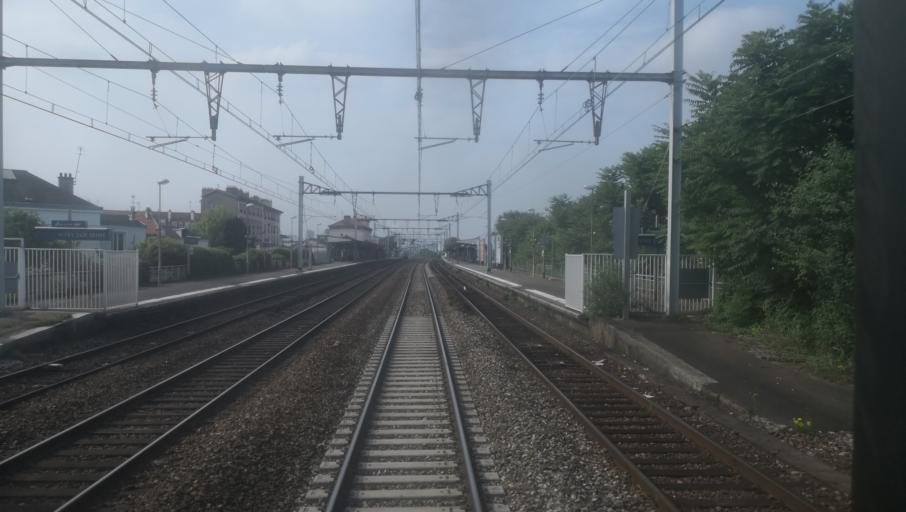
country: FR
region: Ile-de-France
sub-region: Departement du Val-de-Marne
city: Vitry-sur-Seine
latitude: 48.7991
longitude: 2.4034
